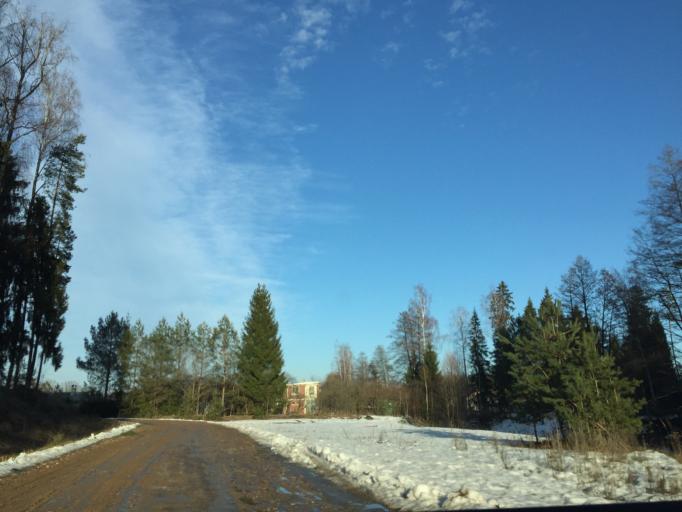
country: LV
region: Lecava
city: Iecava
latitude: 56.6896
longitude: 24.0776
